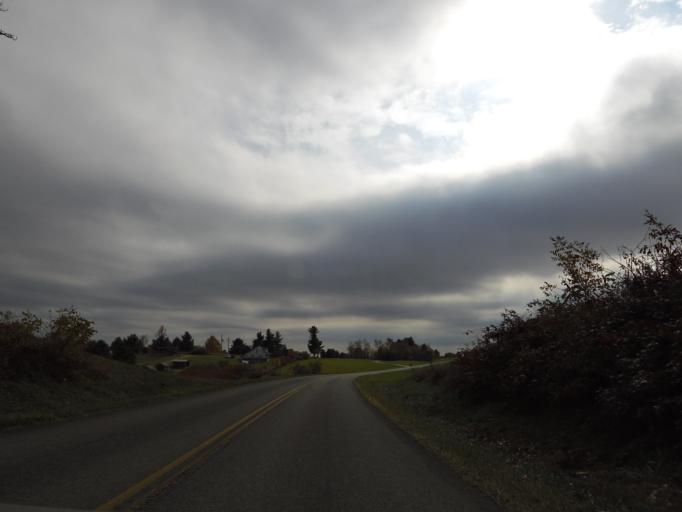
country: US
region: Virginia
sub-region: Carroll County
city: Cana
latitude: 36.6427
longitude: -80.7272
